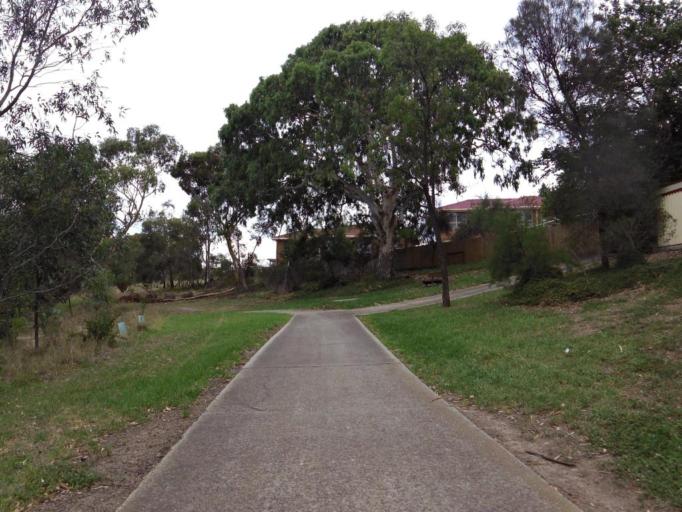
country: AU
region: Victoria
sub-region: Hume
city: Attwood
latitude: -37.6692
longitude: 144.8994
